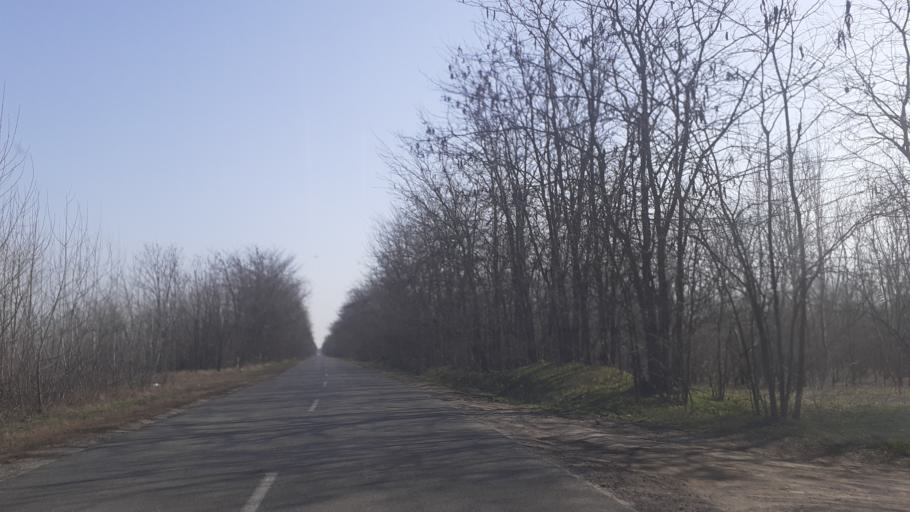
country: HU
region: Bacs-Kiskun
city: Lajosmizse
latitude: 46.9945
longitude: 19.5382
